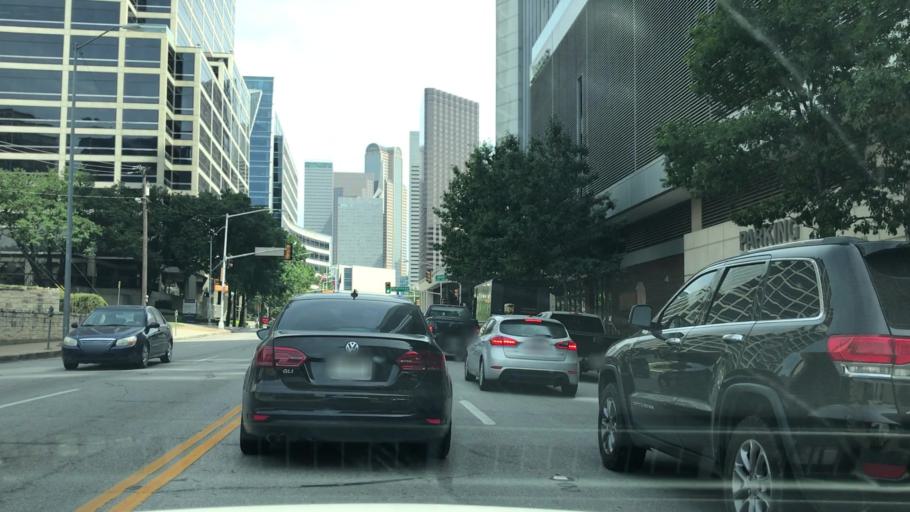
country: US
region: Texas
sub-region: Dallas County
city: Dallas
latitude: 32.7892
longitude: -96.8049
